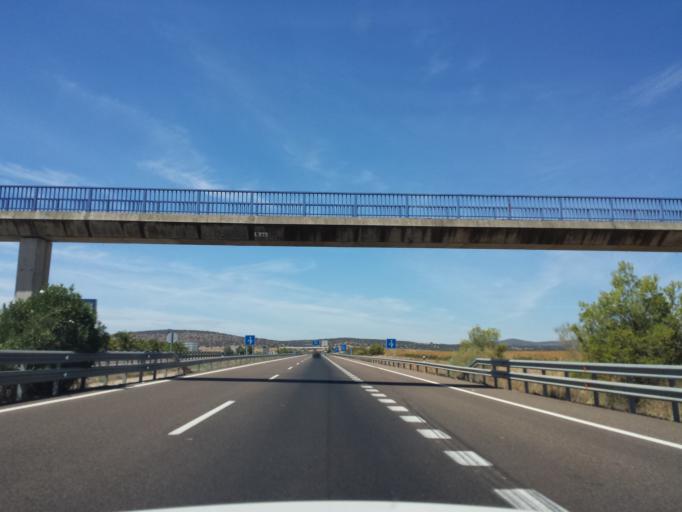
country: ES
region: Extremadura
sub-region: Provincia de Badajoz
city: San Pedro de Merida
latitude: 38.9907
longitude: -6.1129
